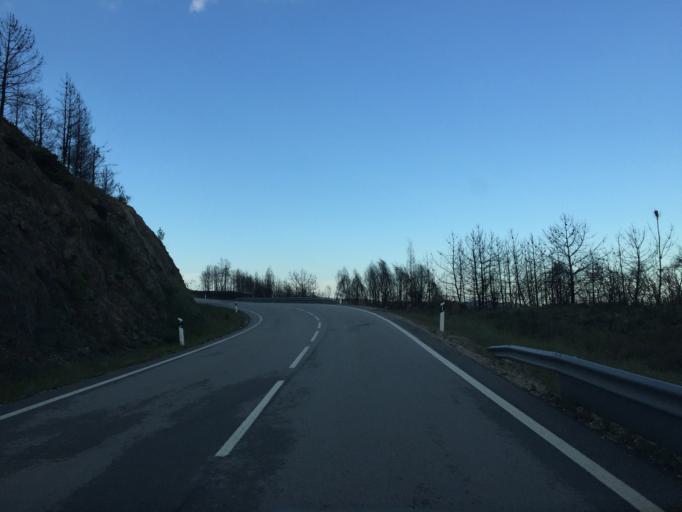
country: PT
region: Coimbra
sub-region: Gois
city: Gois
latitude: 40.0959
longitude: -8.0538
